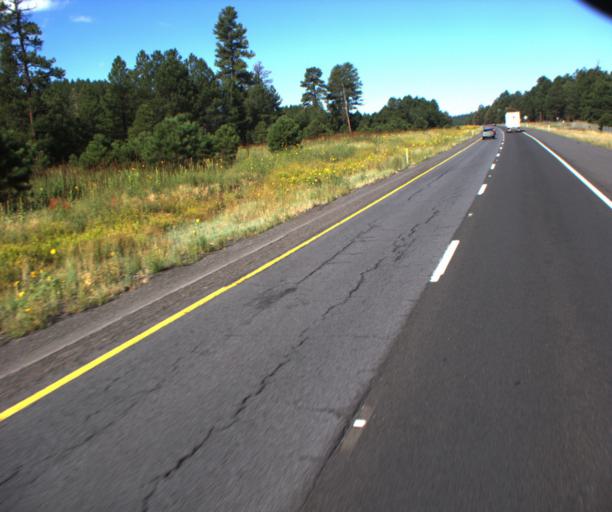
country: US
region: Arizona
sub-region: Coconino County
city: Parks
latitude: 35.2495
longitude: -111.8677
